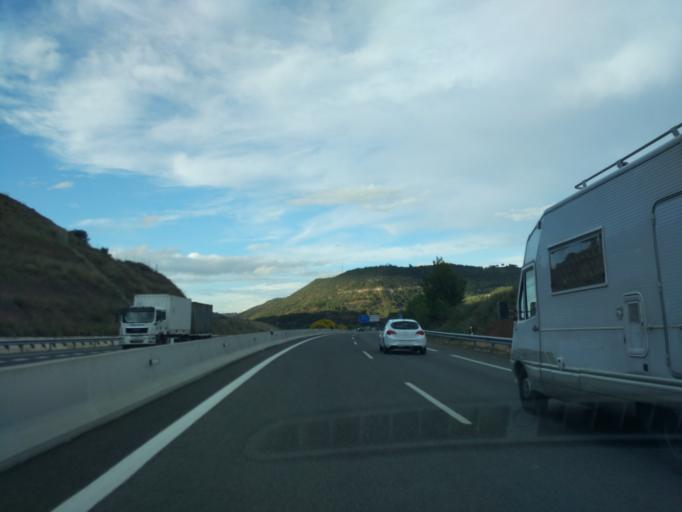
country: ES
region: Castille-La Mancha
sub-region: Provincia de Guadalajara
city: Tortola de Henares
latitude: 40.6828
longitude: -3.0941
